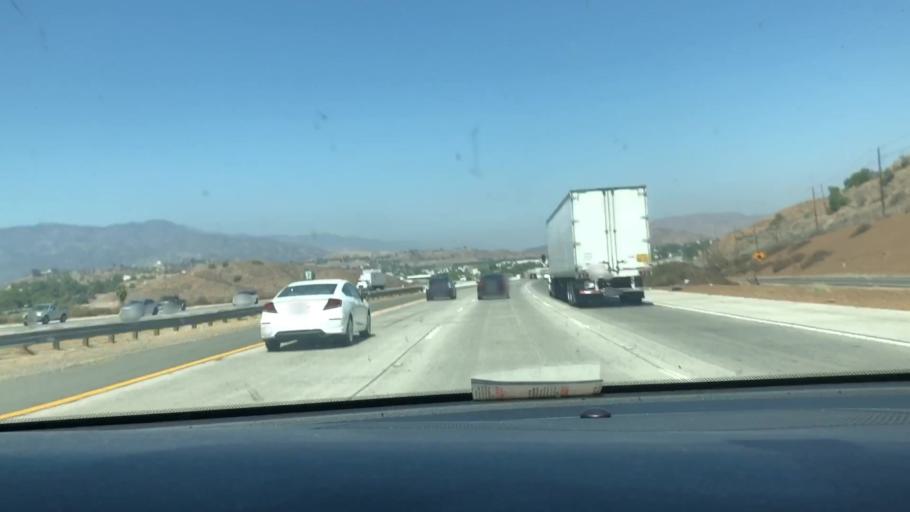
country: US
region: California
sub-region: Riverside County
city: Lake Elsinore
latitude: 33.6755
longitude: -117.3205
